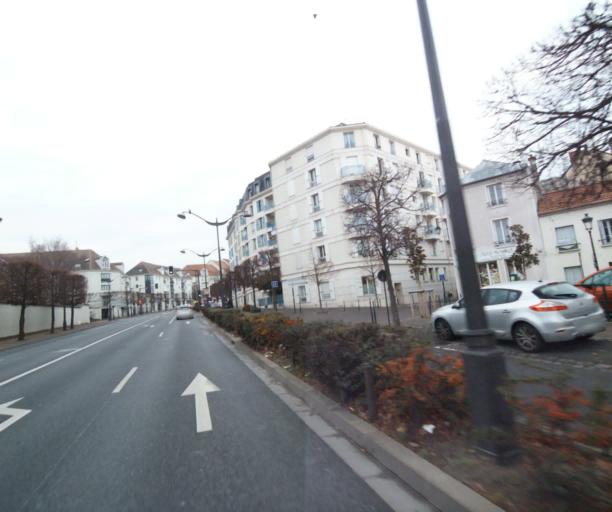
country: FR
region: Ile-de-France
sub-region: Departement des Hauts-de-Seine
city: Rueil-Malmaison
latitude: 48.8793
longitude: 2.1859
